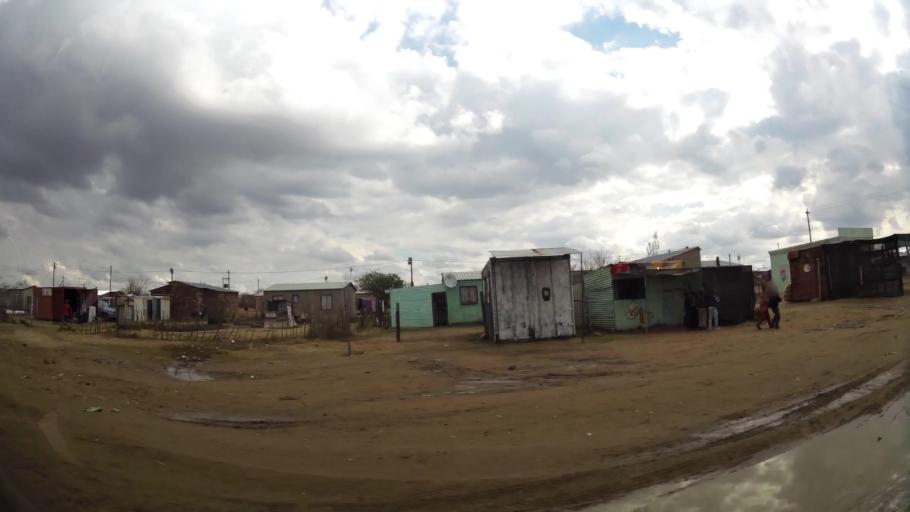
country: ZA
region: Orange Free State
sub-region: Fezile Dabi District Municipality
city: Sasolburg
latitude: -26.8756
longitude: 27.8734
